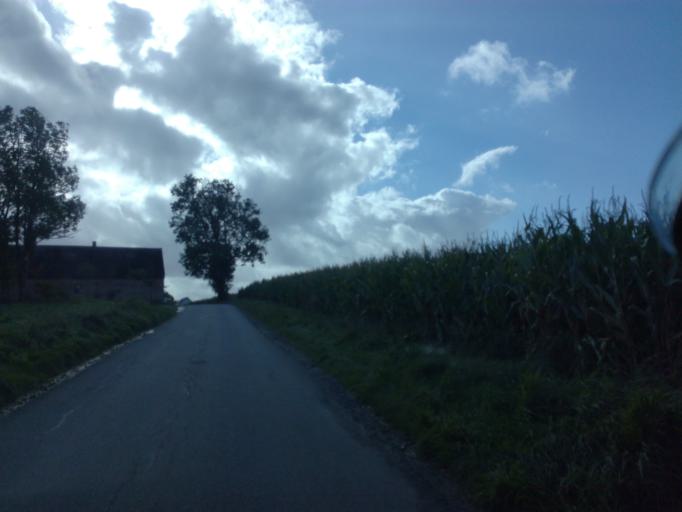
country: DK
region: South Denmark
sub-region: Vejle Kommune
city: Brejning
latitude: 55.6340
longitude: 9.7171
